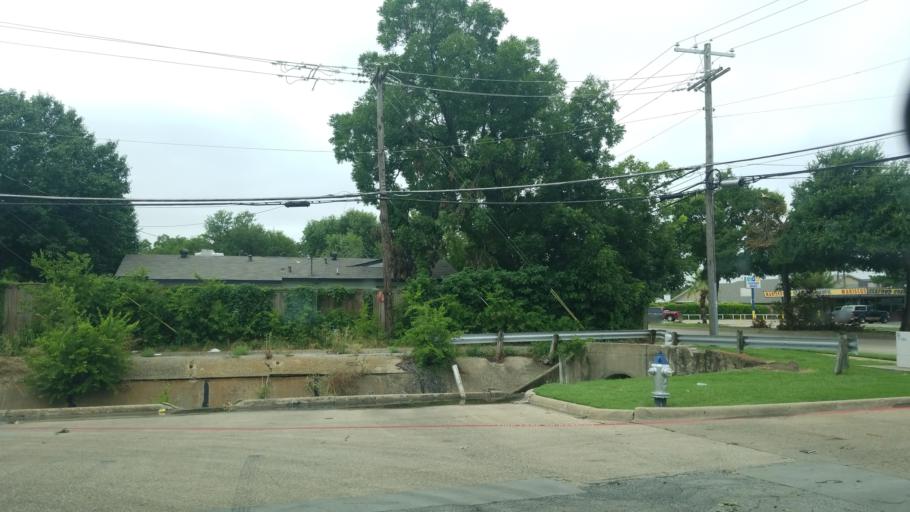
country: US
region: Texas
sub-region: Dallas County
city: Farmers Branch
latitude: 32.9083
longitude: -96.8720
